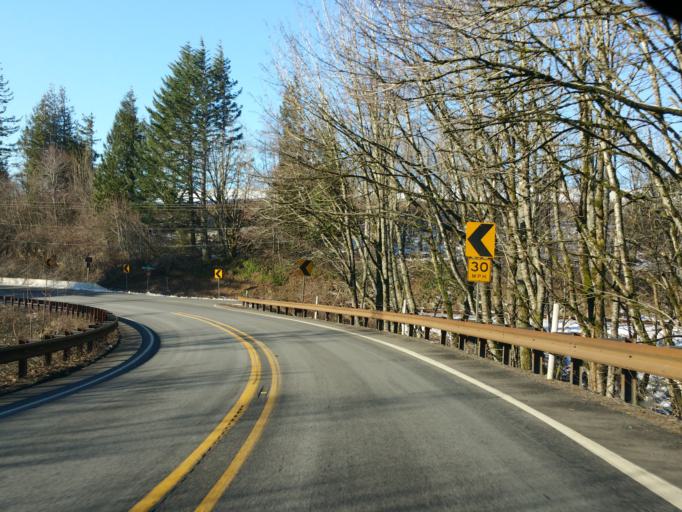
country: US
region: Washington
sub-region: Clark County
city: Washougal
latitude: 45.5662
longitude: -122.2177
